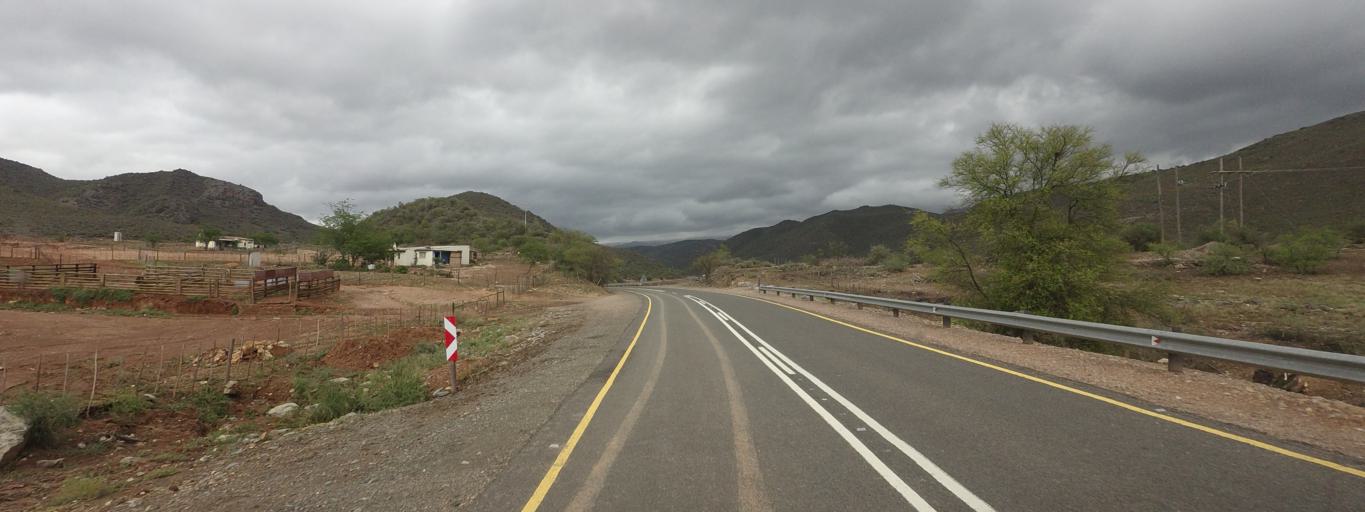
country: ZA
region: Western Cape
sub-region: Eden District Municipality
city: Oudtshoorn
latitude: -33.4116
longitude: 22.2348
